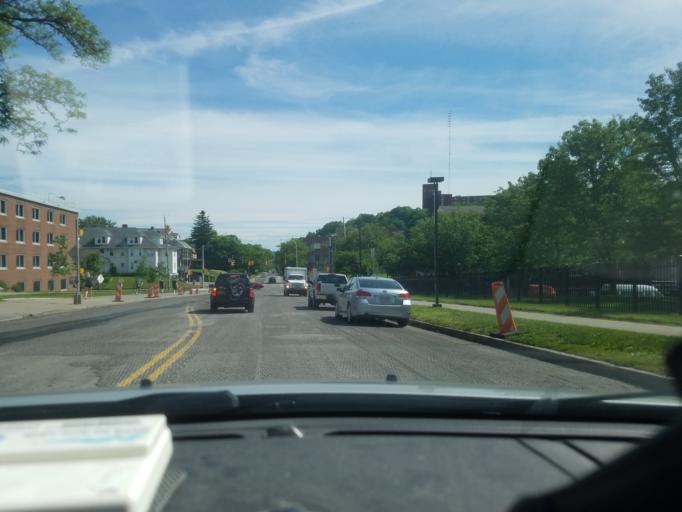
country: US
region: New York
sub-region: Onondaga County
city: Syracuse
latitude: 43.0372
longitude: -76.1300
